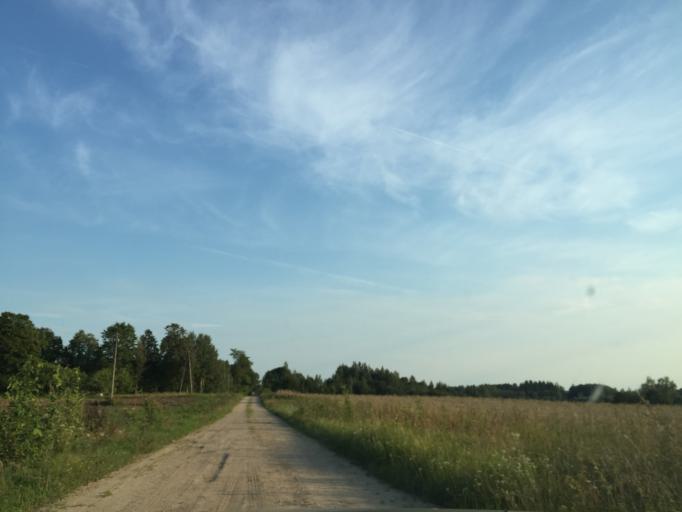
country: LV
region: Limbazu Rajons
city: Limbazi
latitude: 57.5694
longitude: 24.7709
